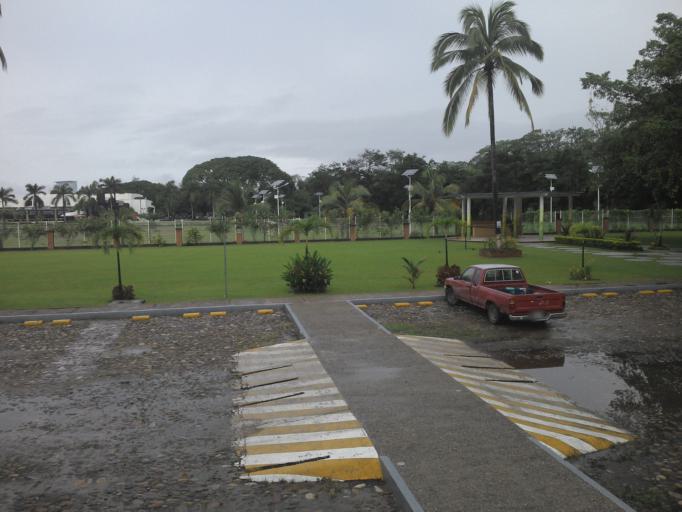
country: MX
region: Jalisco
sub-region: Puerto Vallarta
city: Puerto Vallarta
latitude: 20.6435
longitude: -105.2346
